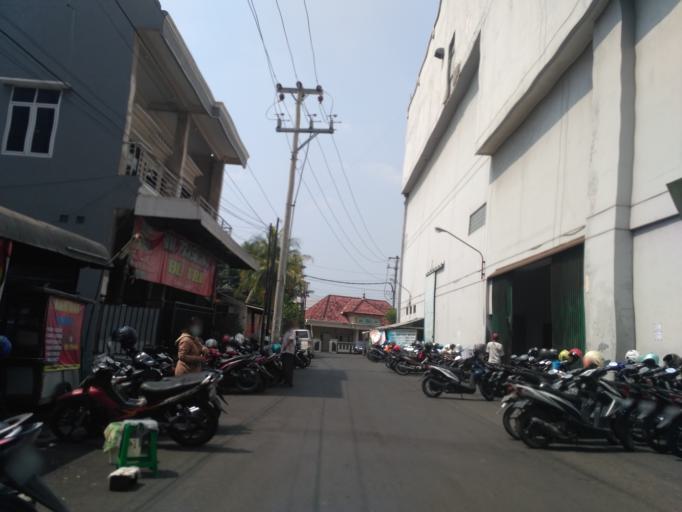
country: ID
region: Central Java
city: Semarang
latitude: -7.0059
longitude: 110.4327
